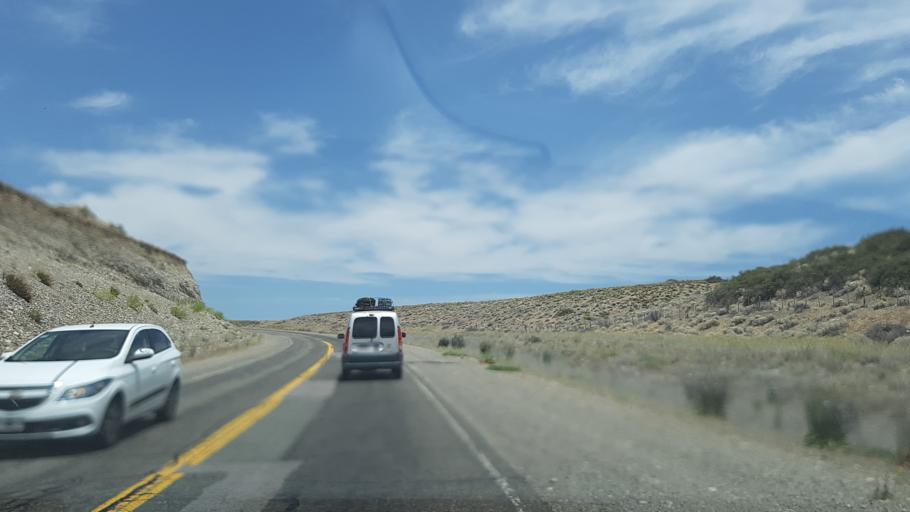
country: AR
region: Rio Negro
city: Pilcaniyeu
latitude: -40.4872
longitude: -70.6803
